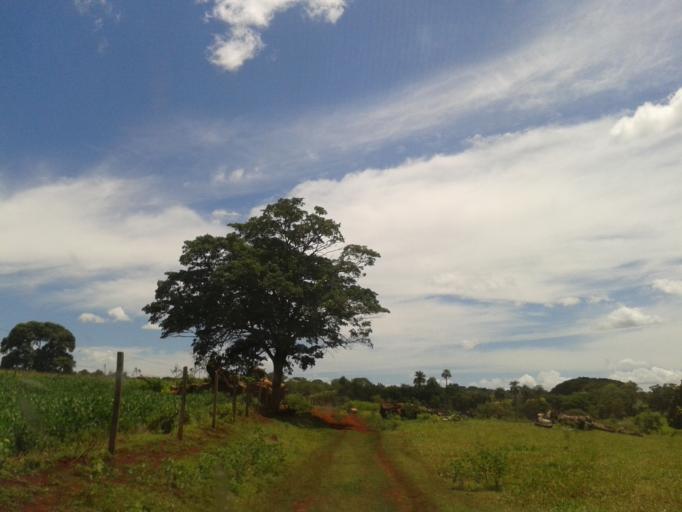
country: BR
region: Minas Gerais
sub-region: Capinopolis
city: Capinopolis
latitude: -18.7763
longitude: -49.8134
